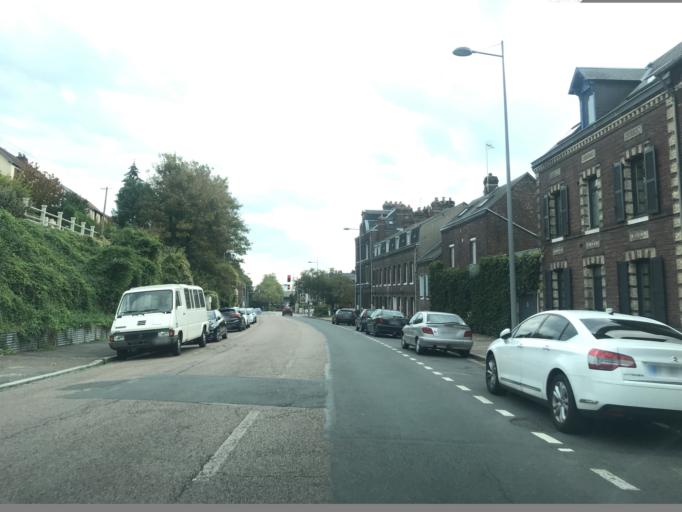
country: FR
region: Haute-Normandie
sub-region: Departement de la Seine-Maritime
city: Deville-les-Rouen
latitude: 49.4545
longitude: 1.0561
